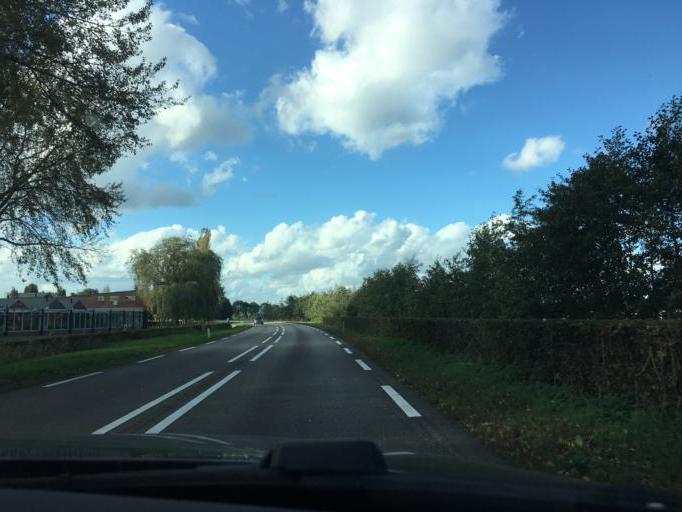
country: NL
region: North Brabant
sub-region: Gemeente Veghel
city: Eerde
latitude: 51.6057
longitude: 5.4996
